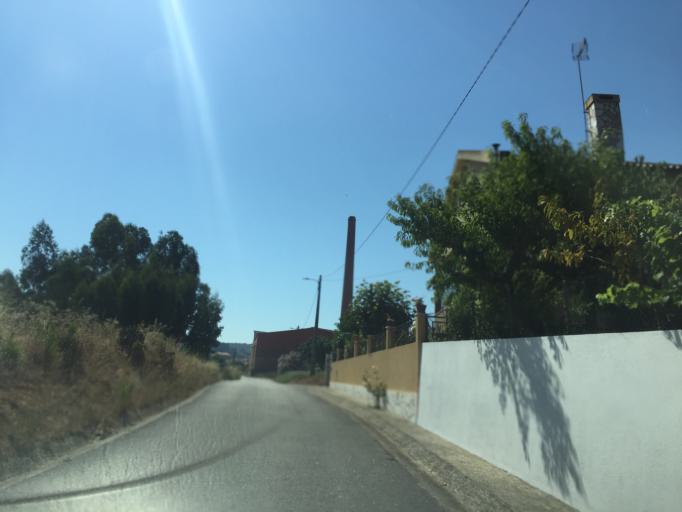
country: PT
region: Santarem
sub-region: Constancia
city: Constancia
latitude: 39.5384
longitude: -8.3187
